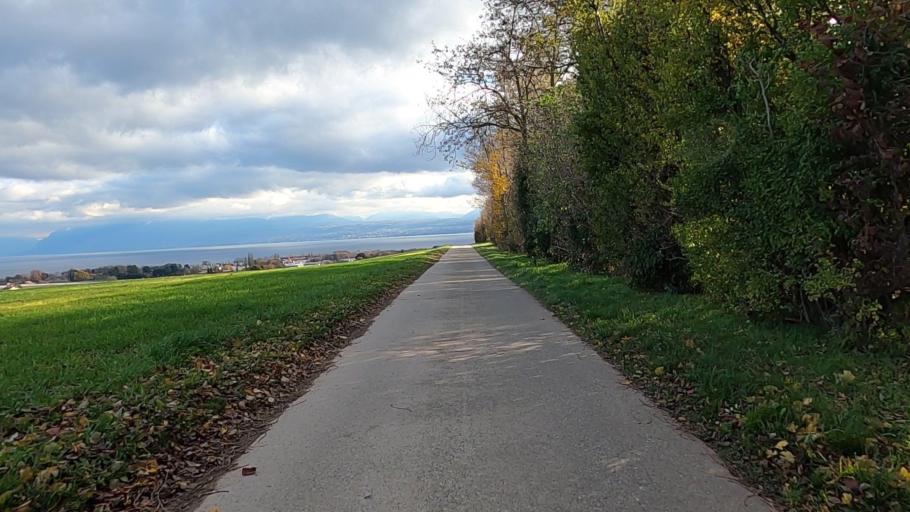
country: CH
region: Vaud
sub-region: Morges District
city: Saint-Prex
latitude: 46.5102
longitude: 6.4578
